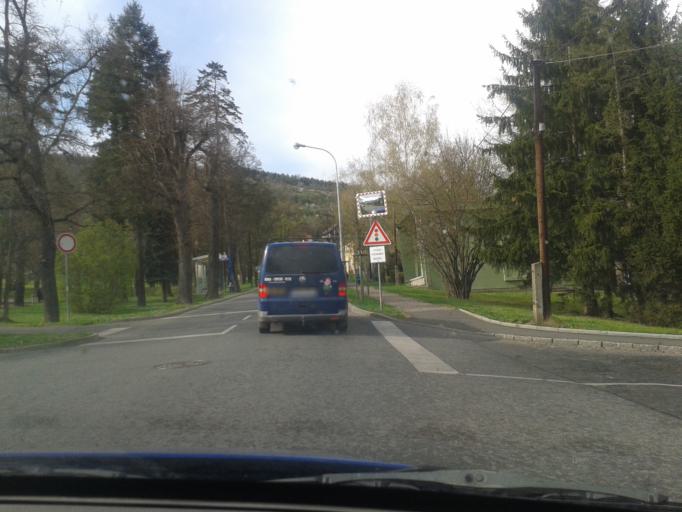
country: CZ
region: Central Bohemia
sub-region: Okres Beroun
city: Beroun
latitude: 49.9663
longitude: 14.0616
